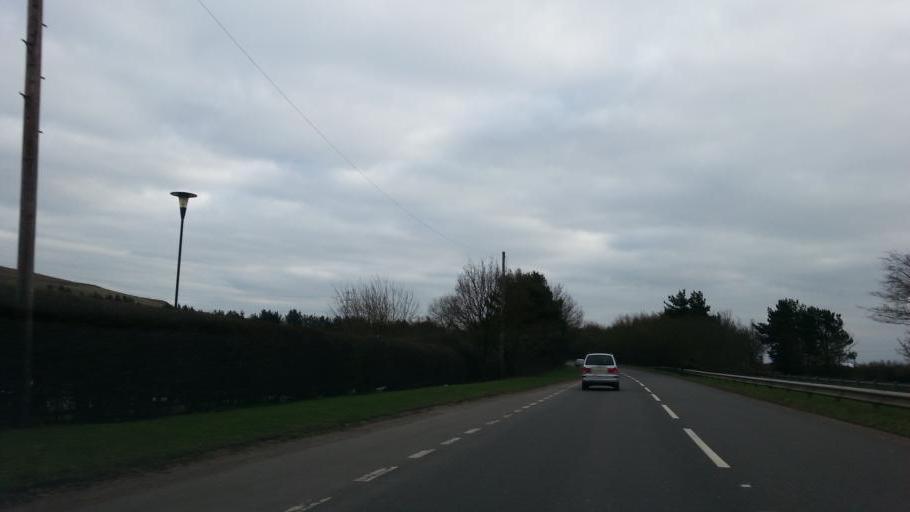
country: GB
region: England
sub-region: Solihull
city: Bickenhill
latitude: 52.4616
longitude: -1.7056
